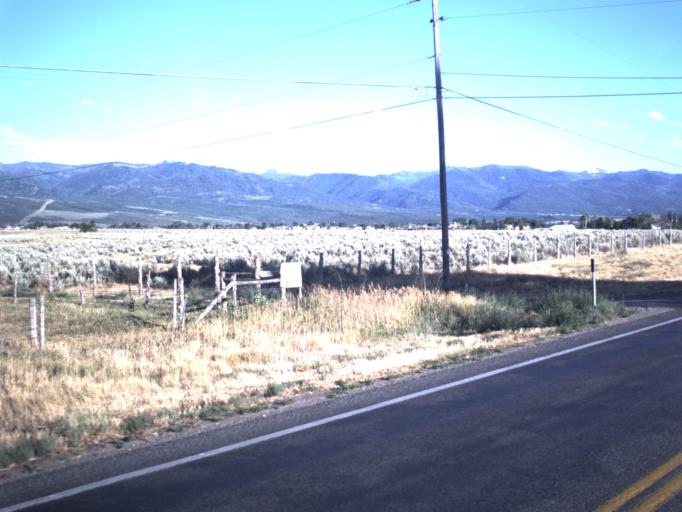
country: US
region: Utah
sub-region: Sanpete County
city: Mount Pleasant
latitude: 39.5619
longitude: -111.4555
